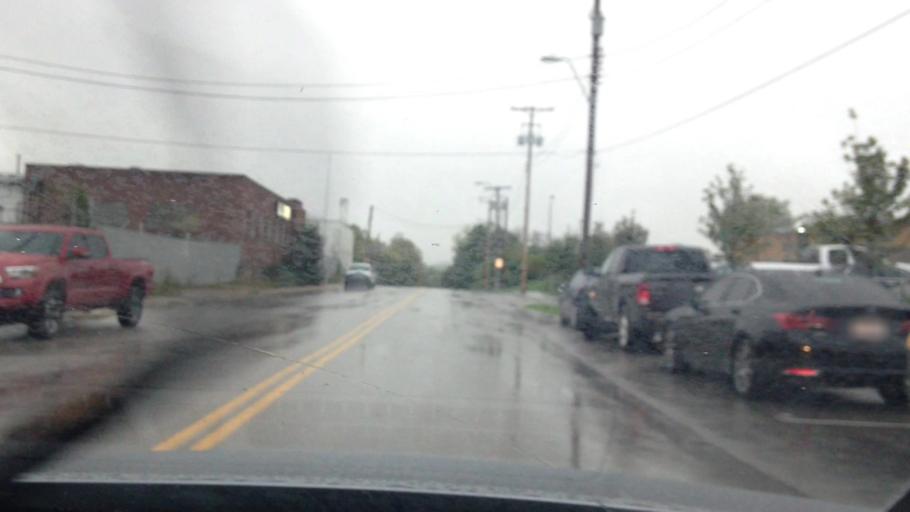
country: US
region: Missouri
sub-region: Jackson County
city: Kansas City
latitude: 39.1113
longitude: -94.5762
